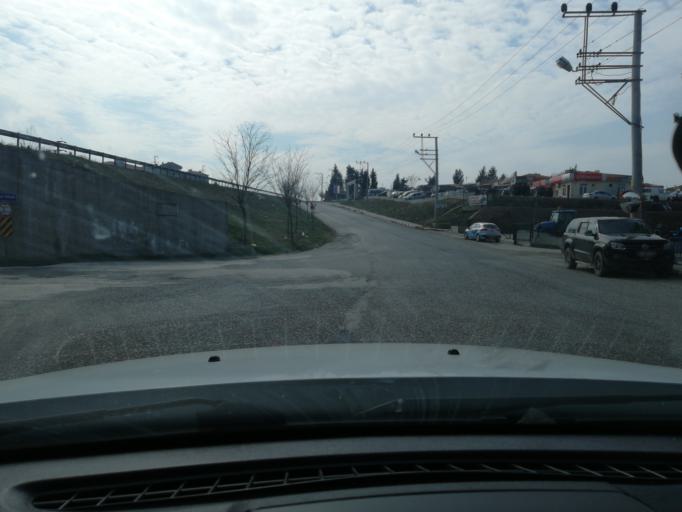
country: TR
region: Edirne
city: Kesan
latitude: 40.8689
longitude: 26.6279
